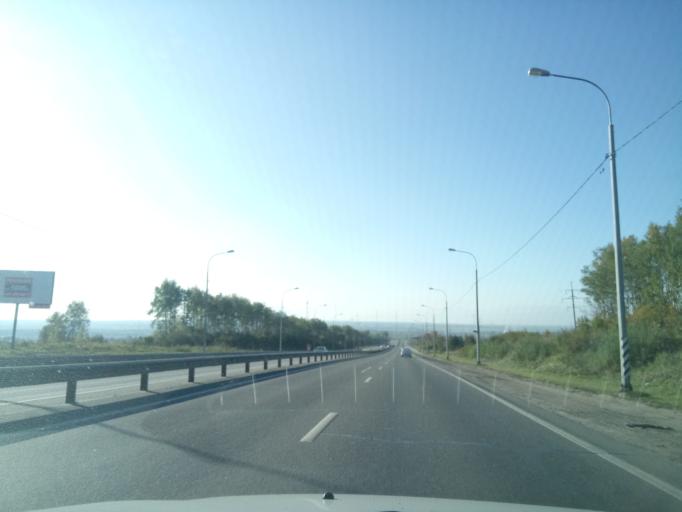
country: RU
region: Nizjnij Novgorod
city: Nizhniy Novgorod
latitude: 56.2033
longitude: 43.9258
